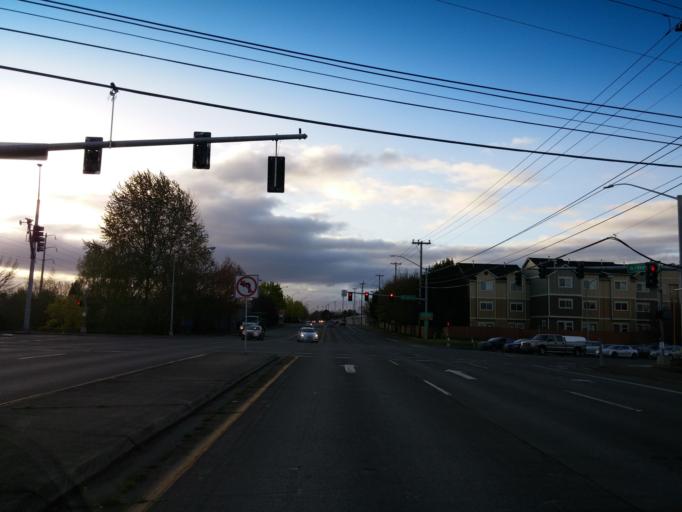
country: US
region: Oregon
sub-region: Washington County
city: Aloha
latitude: 45.5157
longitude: -122.8679
